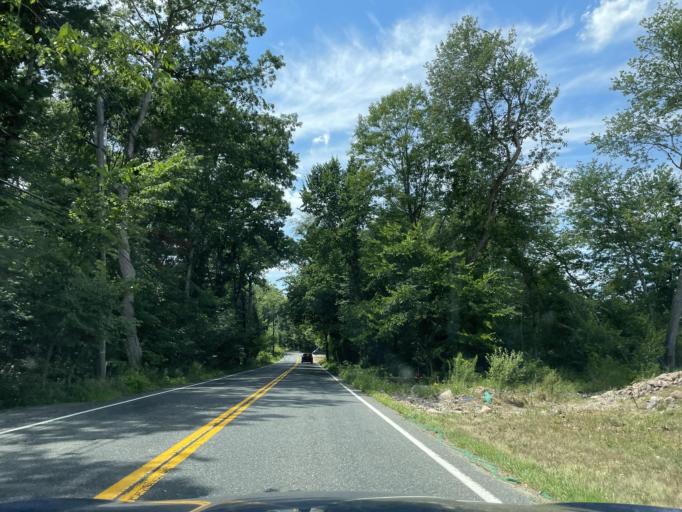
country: US
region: Massachusetts
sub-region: Middlesex County
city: Natick
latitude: 42.2551
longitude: -71.3463
